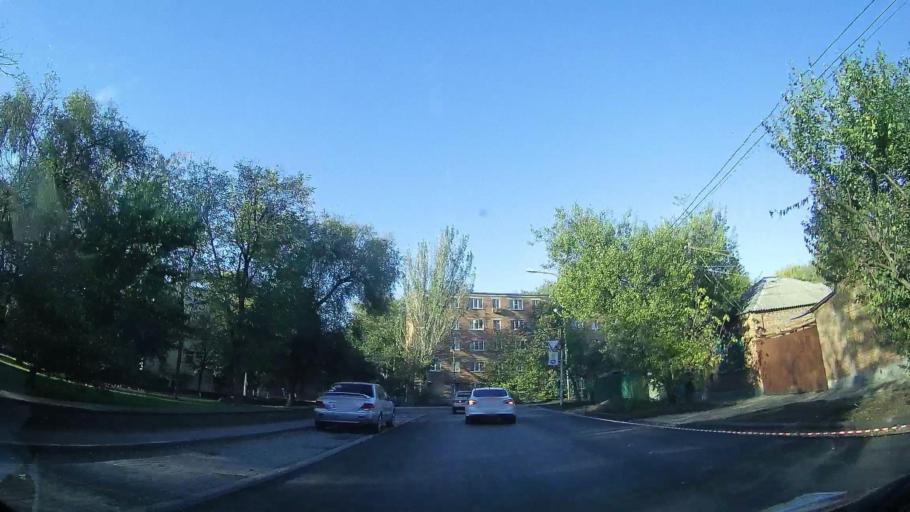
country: RU
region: Rostov
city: Rostov-na-Donu
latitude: 47.2397
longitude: 39.6974
